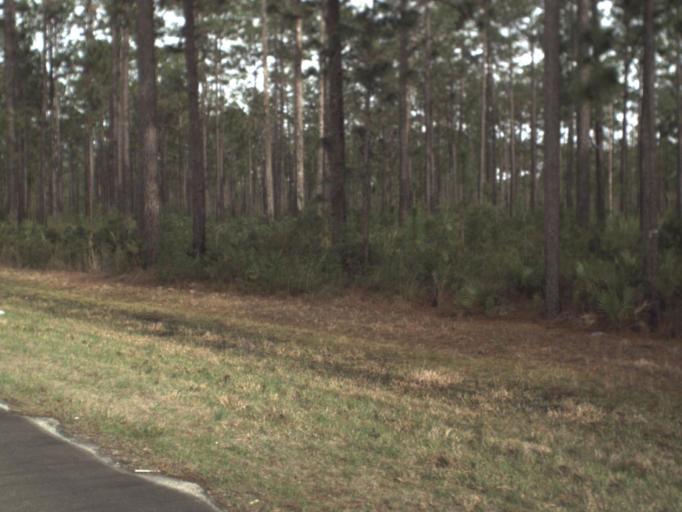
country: US
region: Florida
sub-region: Gulf County
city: Wewahitchka
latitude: 30.1397
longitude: -85.3320
